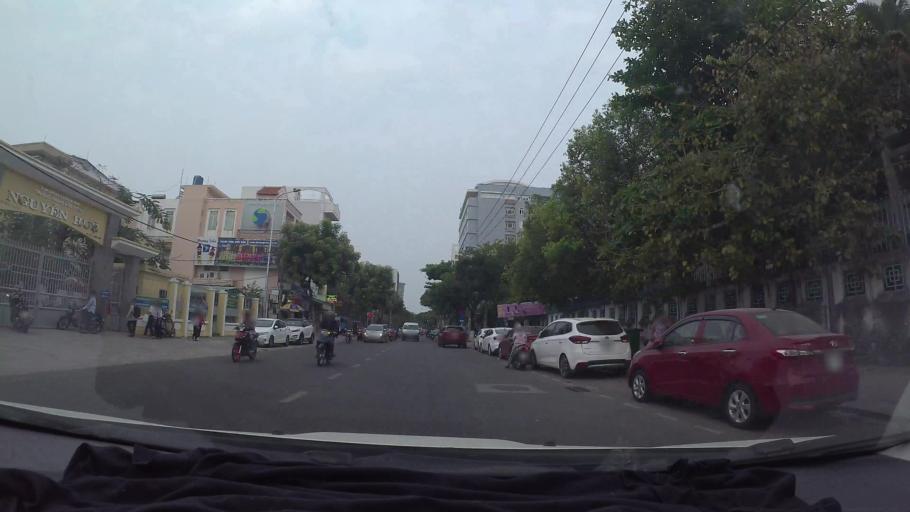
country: VN
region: Da Nang
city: Da Nang
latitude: 16.0740
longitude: 108.2161
